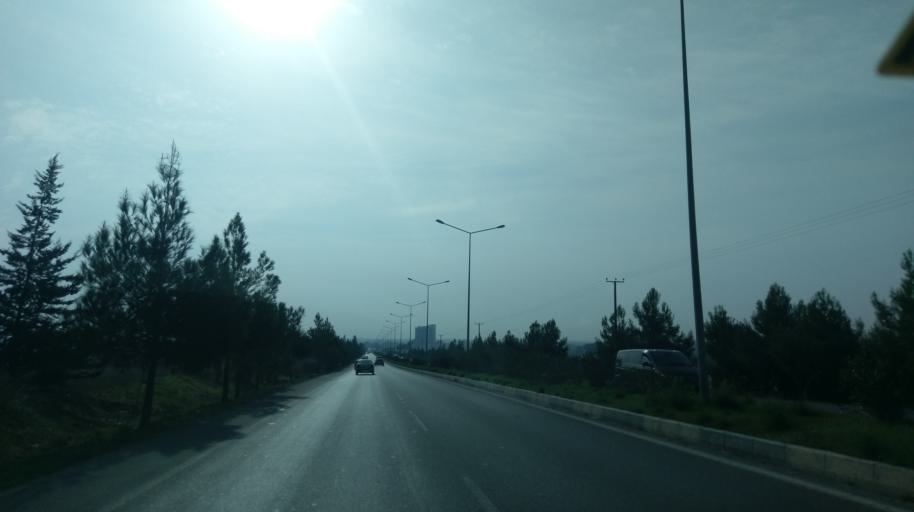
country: CY
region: Lefkosia
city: Nicosia
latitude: 35.2244
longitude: 33.3152
